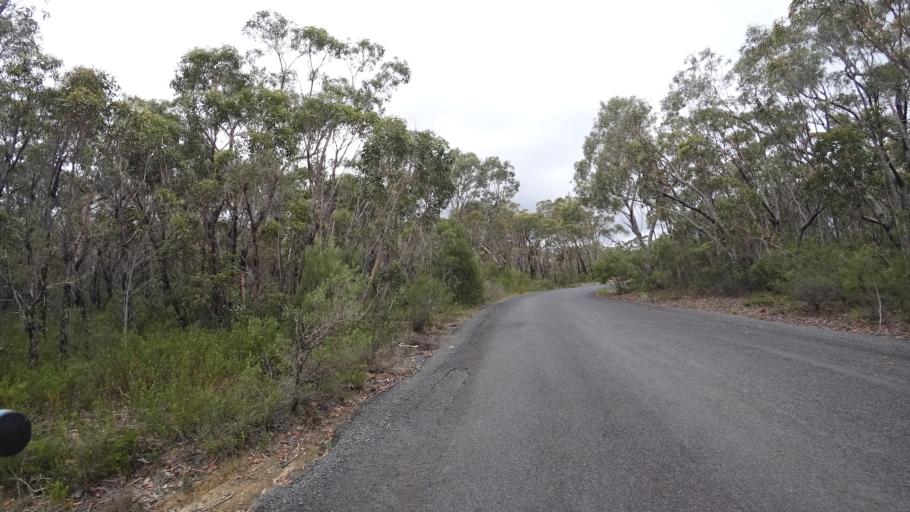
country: AU
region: New South Wales
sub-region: Shoalhaven Shire
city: Milton
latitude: -35.1095
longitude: 150.3334
